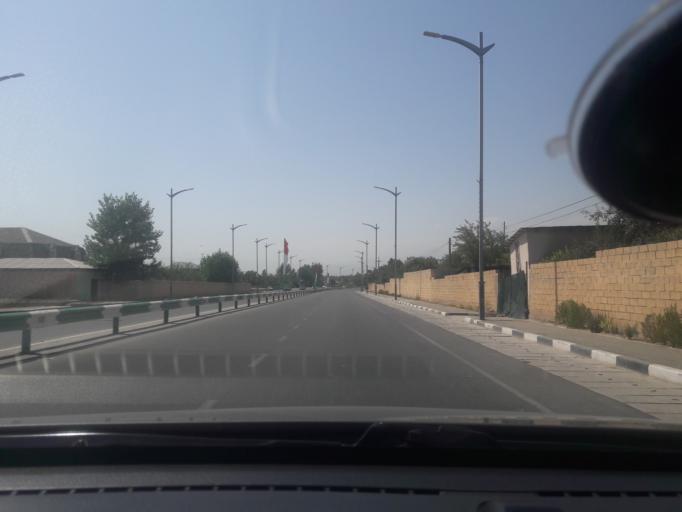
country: TJ
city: Shahrinav
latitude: 38.5624
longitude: 68.4190
